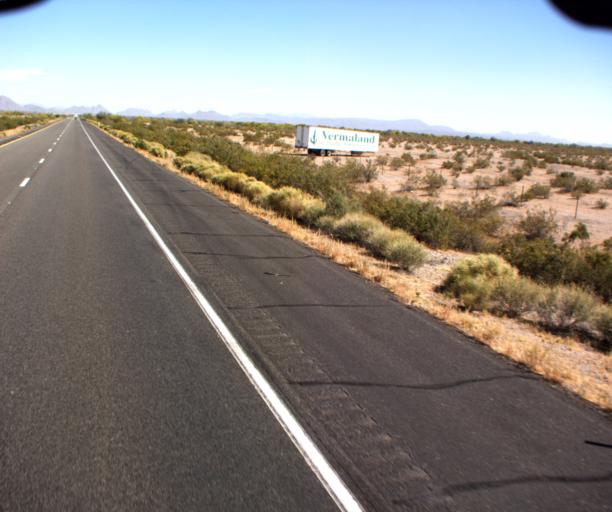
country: US
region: Arizona
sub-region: Maricopa County
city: Gila Bend
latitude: 32.9339
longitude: -112.7112
